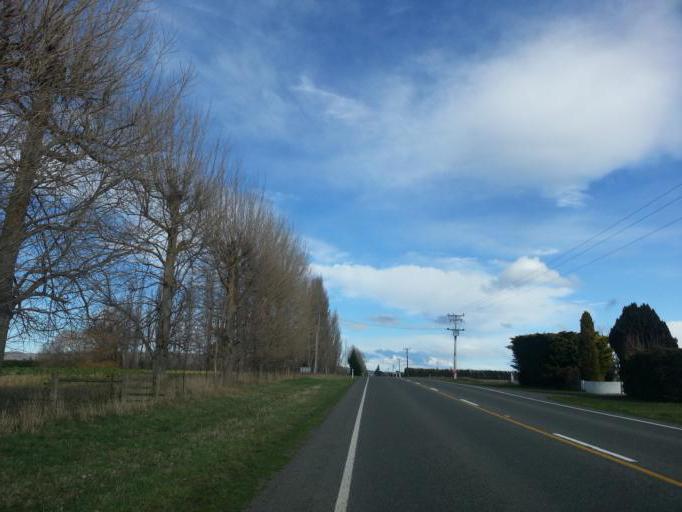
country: NZ
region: Canterbury
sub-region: Hurunui District
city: Amberley
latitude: -42.7800
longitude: 172.8434
